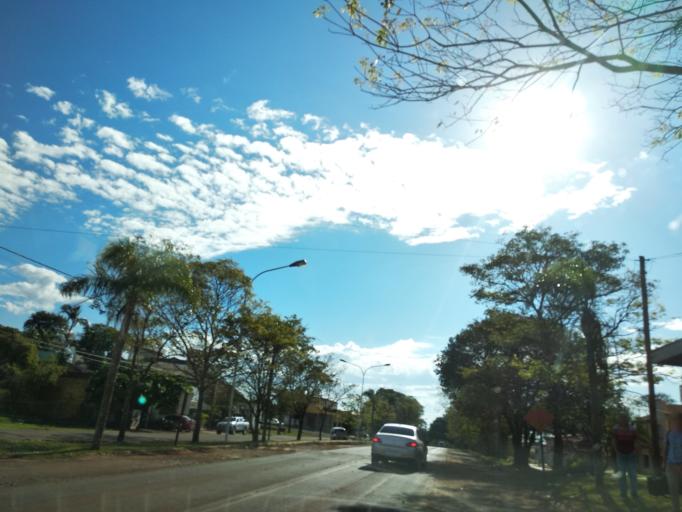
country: AR
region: Misiones
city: Aristobulo del Valle
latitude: -27.0937
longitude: -54.8955
